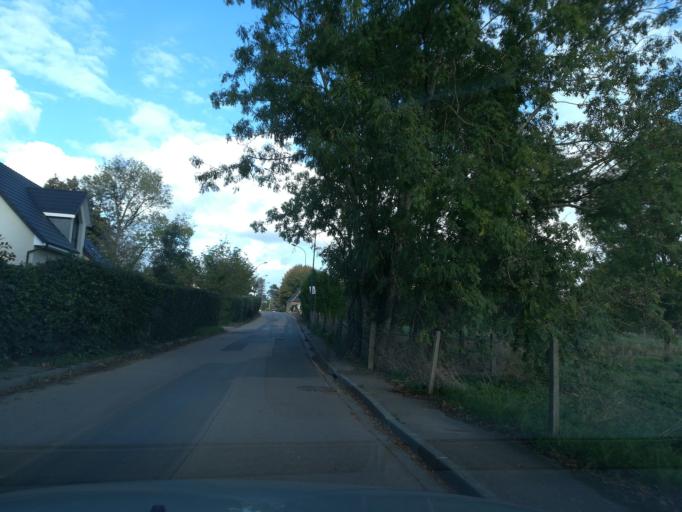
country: FR
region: Haute-Normandie
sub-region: Departement de la Seine-Maritime
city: Bois-Guillaume
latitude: 49.4721
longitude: 1.1309
